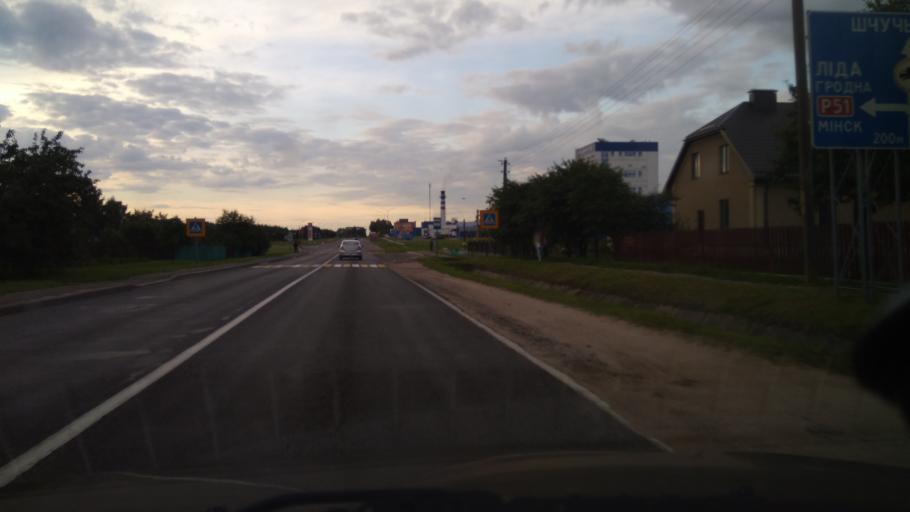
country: BY
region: Grodnenskaya
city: Shchuchin
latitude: 53.5876
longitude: 24.7463
